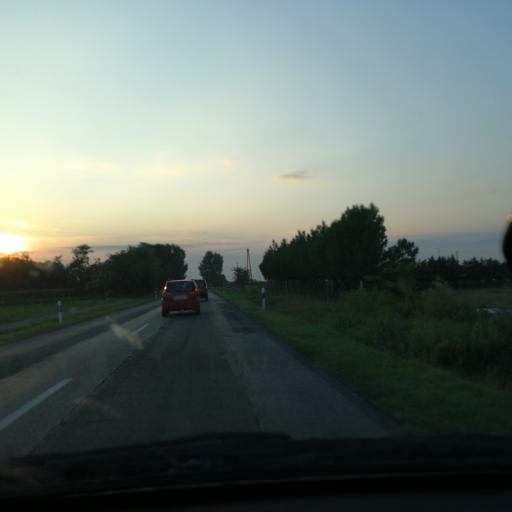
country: HU
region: Bacs-Kiskun
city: Kiskoros
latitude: 46.5928
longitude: 19.3364
